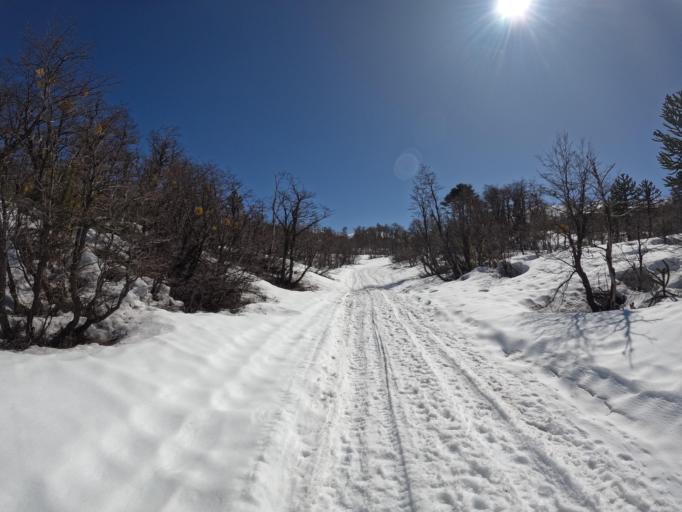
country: CL
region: Araucania
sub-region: Provincia de Cautin
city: Vilcun
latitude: -38.6594
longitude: -71.6186
